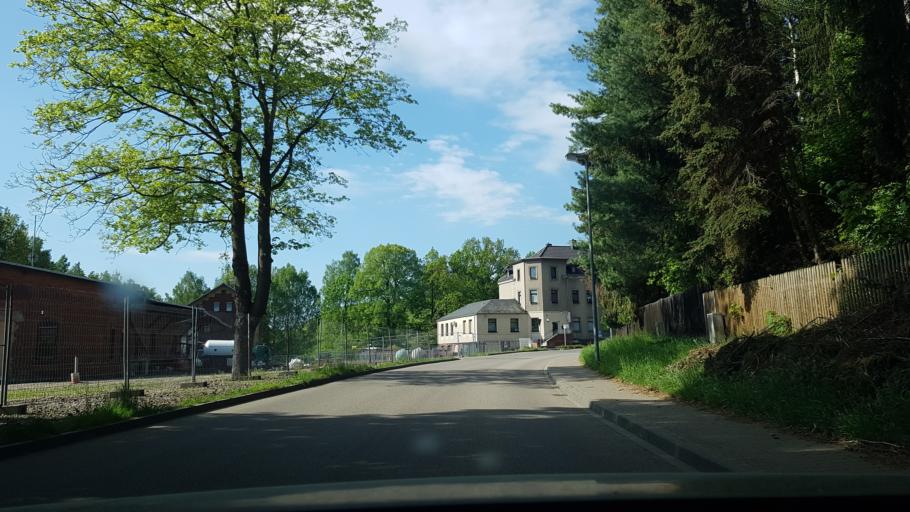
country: DE
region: Saxony
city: Wittgensdorf
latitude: 50.8916
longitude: 12.8904
